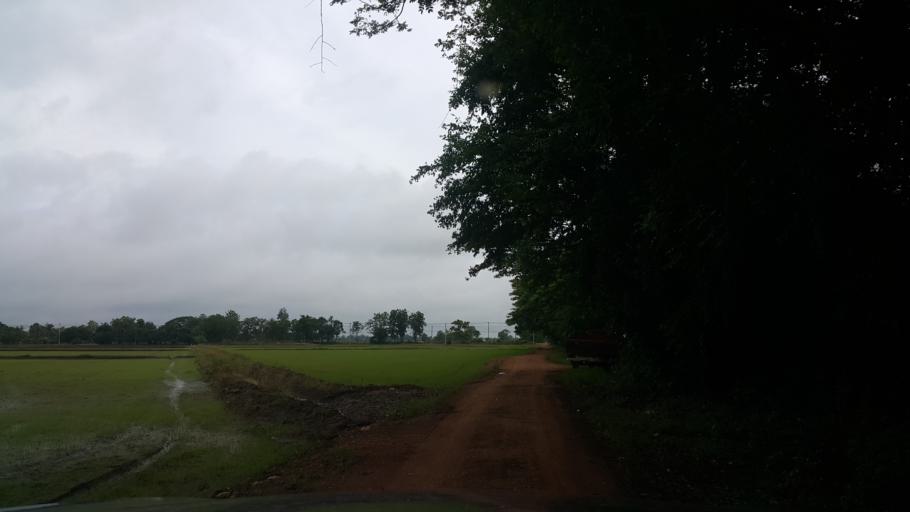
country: TH
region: Sukhothai
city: Sawankhalok
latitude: 17.3068
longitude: 99.7136
